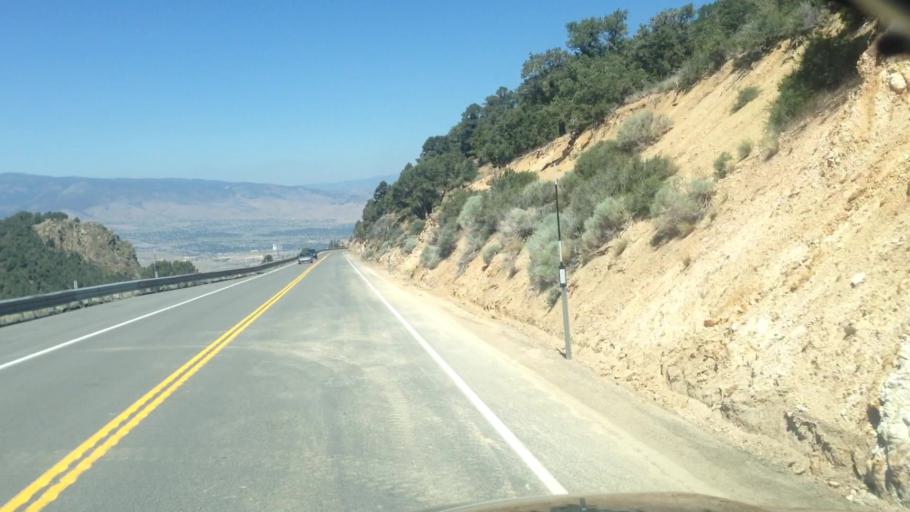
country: US
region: Nevada
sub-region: Storey County
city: Virginia City
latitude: 39.3507
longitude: -119.6564
